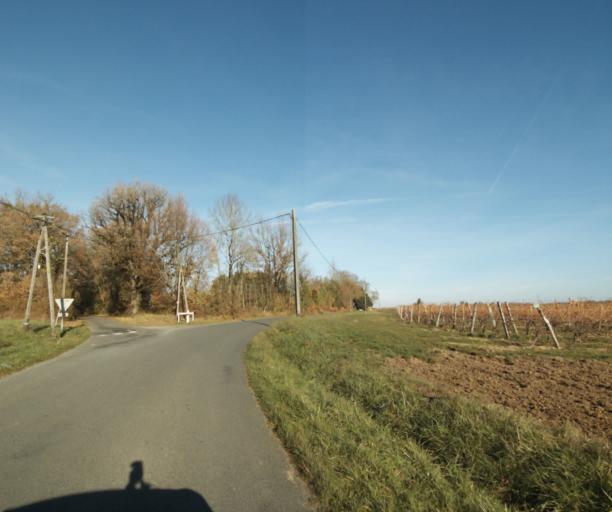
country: FR
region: Poitou-Charentes
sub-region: Departement de la Charente-Maritime
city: Cherac
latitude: 45.7146
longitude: -0.4534
